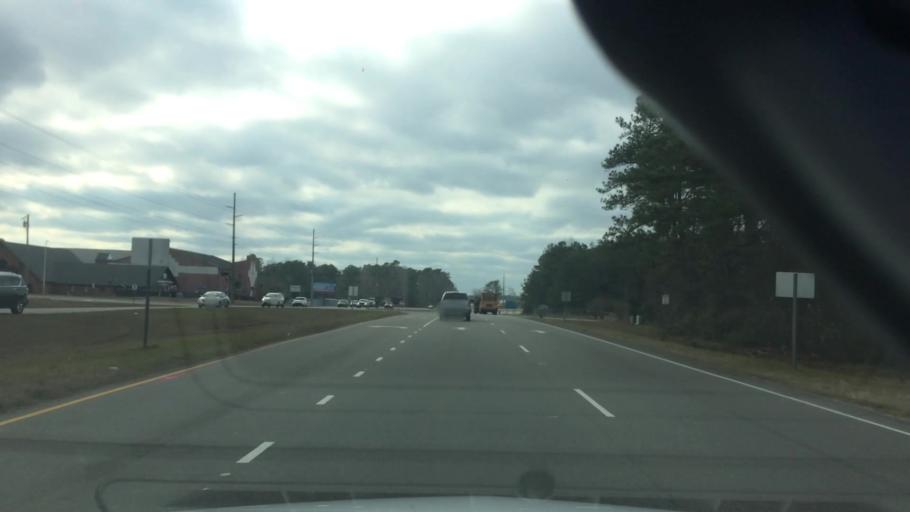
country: US
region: North Carolina
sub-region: Brunswick County
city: Shallotte
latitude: 33.9879
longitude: -78.3577
